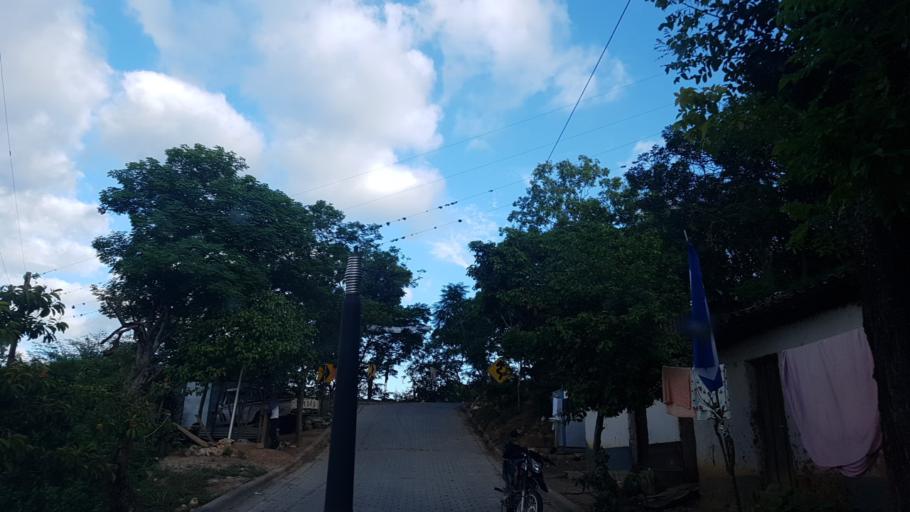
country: NI
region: Nueva Segovia
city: Ocotal
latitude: 13.6520
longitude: -86.6120
